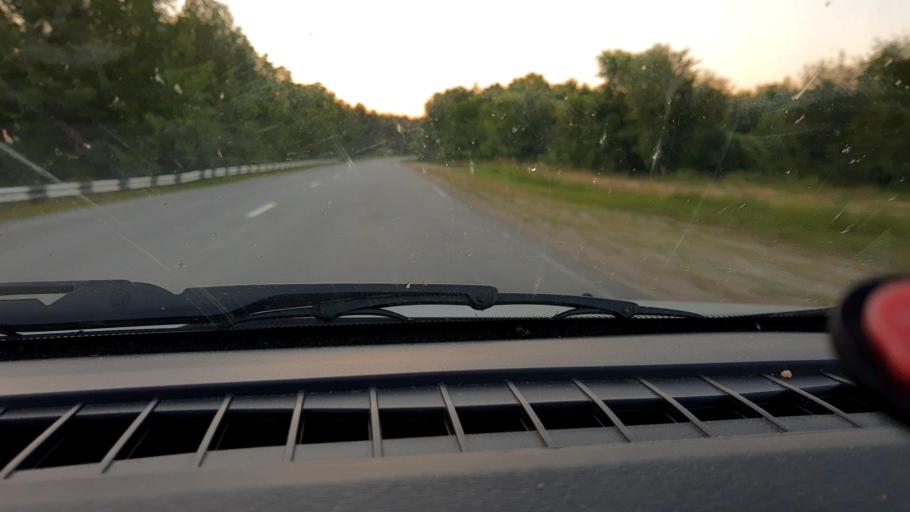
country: RU
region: Nizjnij Novgorod
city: Uren'
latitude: 57.4097
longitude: 45.6838
